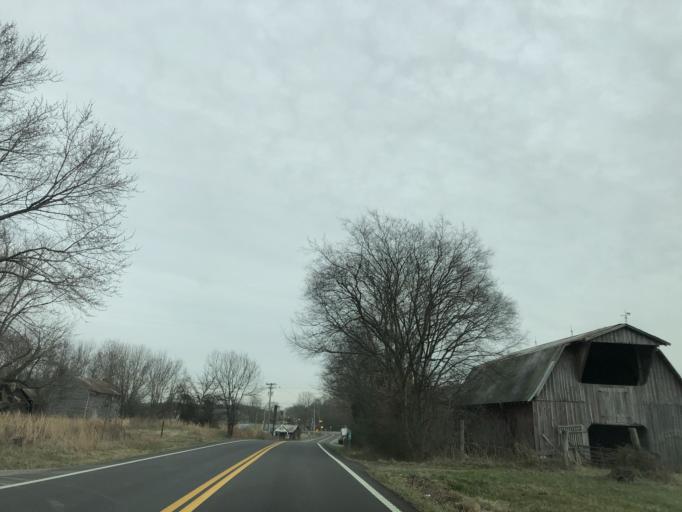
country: US
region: Tennessee
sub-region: Sumner County
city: White House
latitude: 36.4749
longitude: -86.7144
